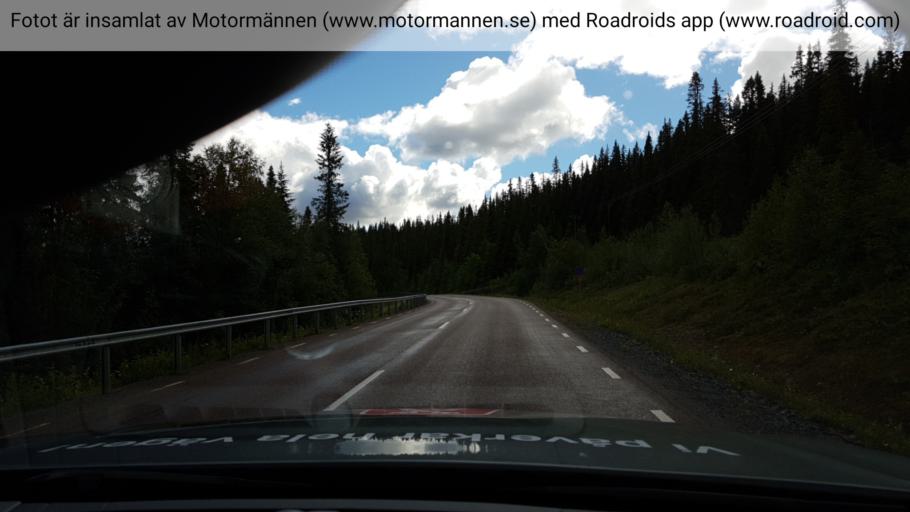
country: SE
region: Jaemtland
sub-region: Are Kommun
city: Jarpen
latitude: 63.0933
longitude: 13.7753
